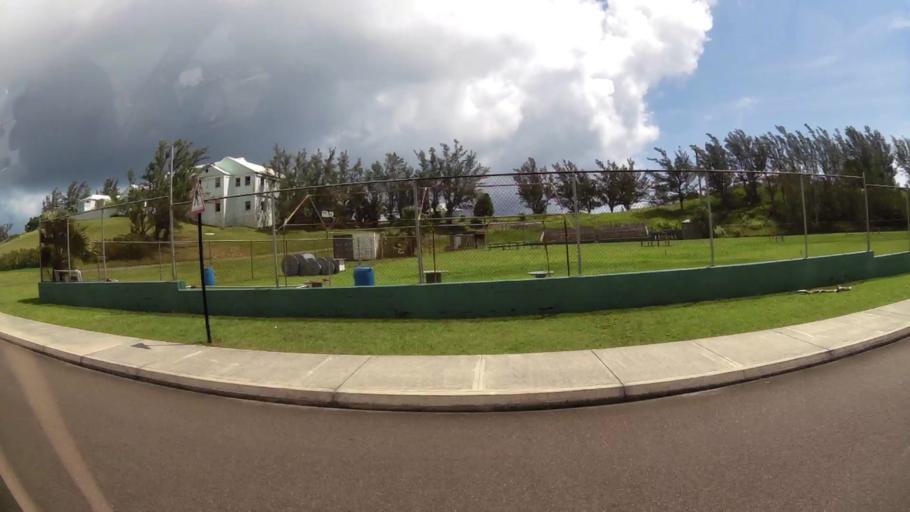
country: BM
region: Saint George
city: Saint George
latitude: 32.3642
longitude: -64.6663
